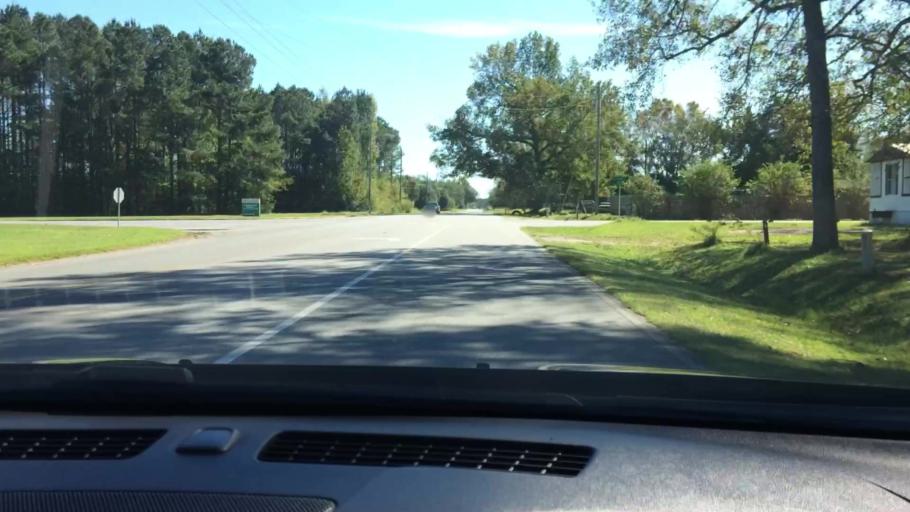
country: US
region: North Carolina
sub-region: Pitt County
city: Grifton
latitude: 35.4060
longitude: -77.4230
